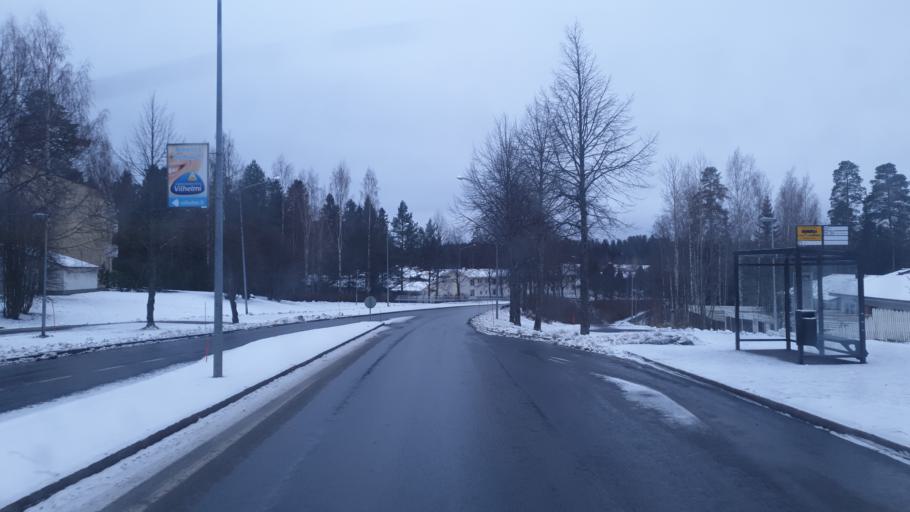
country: FI
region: Northern Savo
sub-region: Kuopio
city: Kuopio
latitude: 62.8387
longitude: 27.6353
